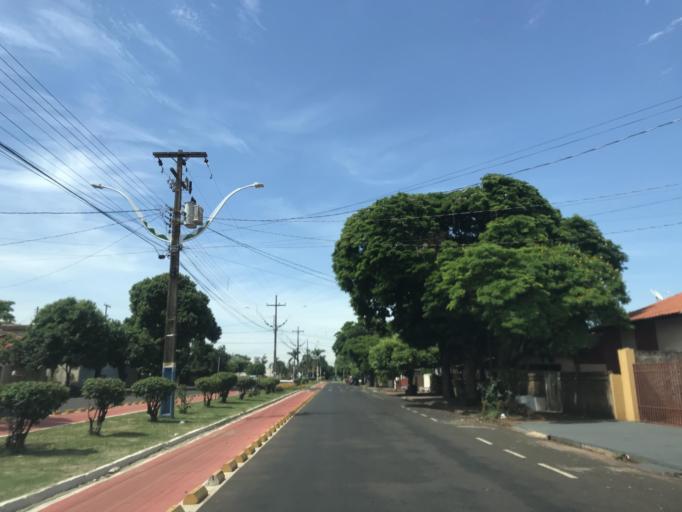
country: BR
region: Parana
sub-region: Terra Rica
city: Terra Rica
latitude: -22.7327
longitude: -52.6246
